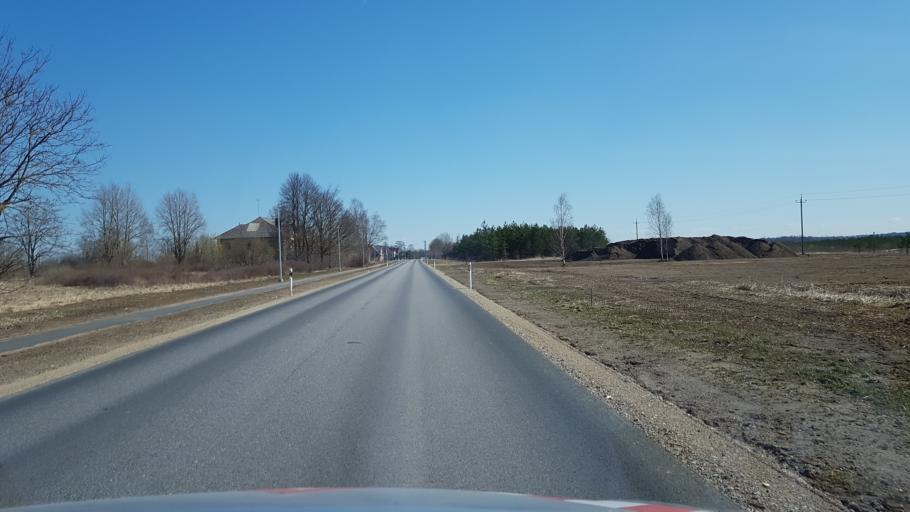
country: EE
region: Ida-Virumaa
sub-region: Kohtla-Nomme vald
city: Kohtla-Nomme
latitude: 59.3553
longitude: 27.2091
